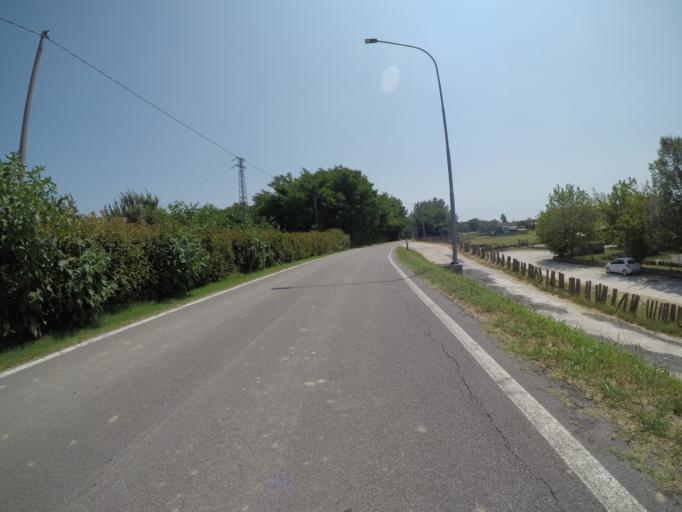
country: IT
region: Veneto
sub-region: Provincia di Rovigo
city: Villamarzana
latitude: 45.0077
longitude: 11.6733
